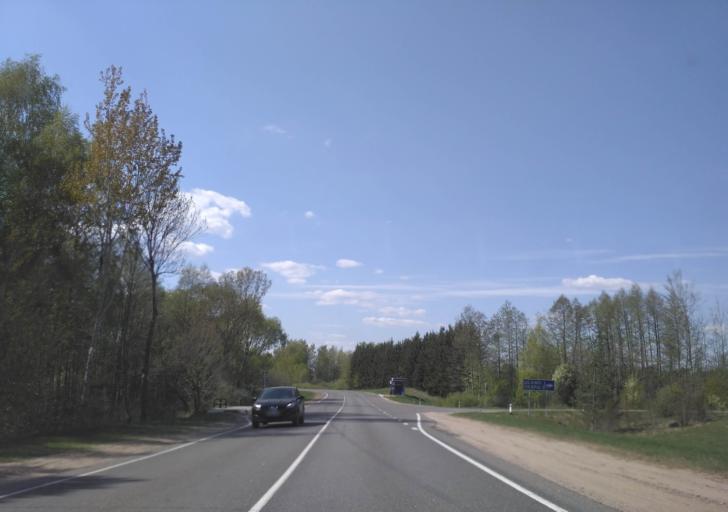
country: BY
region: Minsk
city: Narach
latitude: 54.8885
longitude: 26.7901
